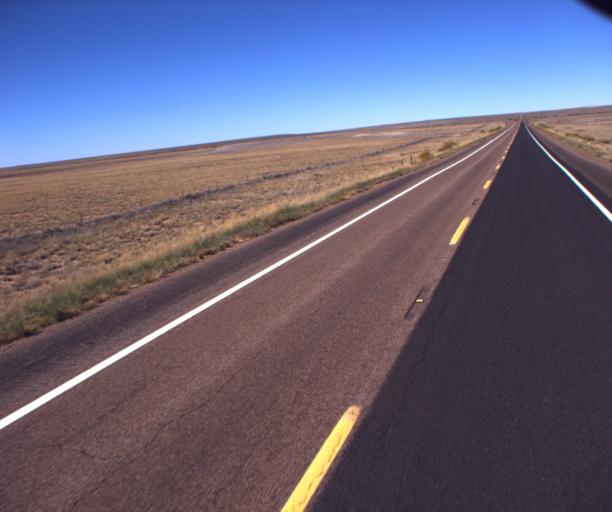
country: US
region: Arizona
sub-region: Navajo County
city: Snowflake
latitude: 34.7240
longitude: -109.7759
